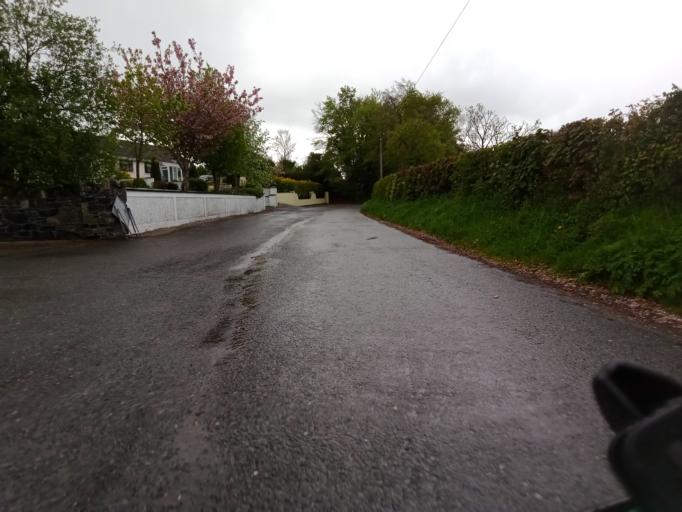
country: IE
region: Leinster
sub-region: Kilkenny
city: Kilkenny
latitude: 52.6840
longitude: -7.2677
